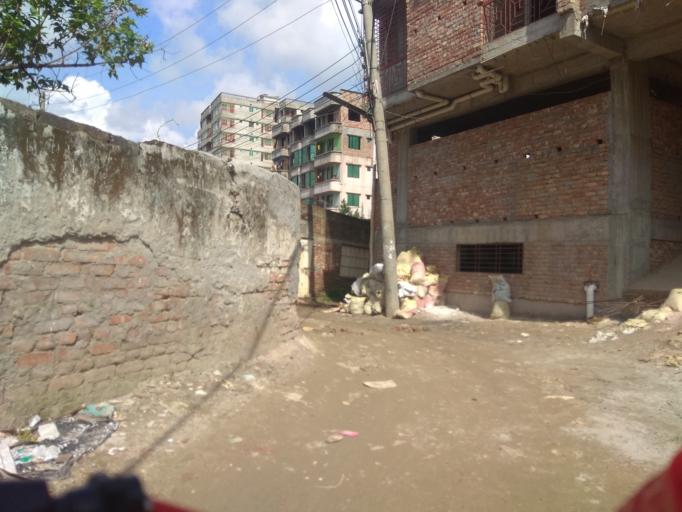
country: BD
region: Dhaka
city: Tungi
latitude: 23.8149
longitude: 90.3870
